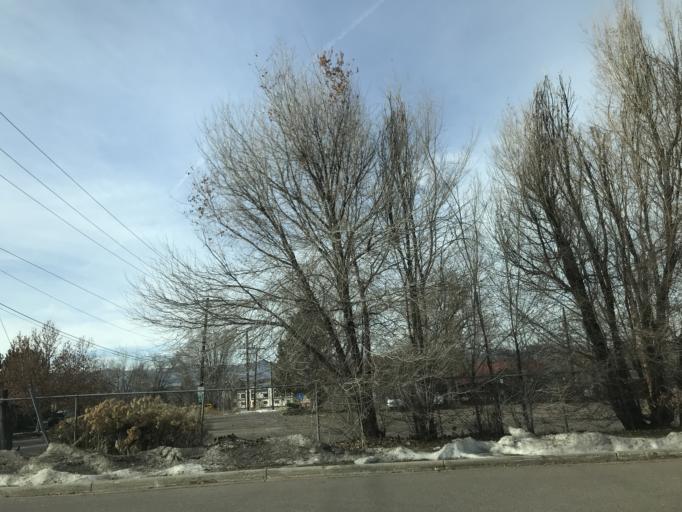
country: US
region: Colorado
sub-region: Arapahoe County
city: Littleton
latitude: 39.6154
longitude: -105.0114
